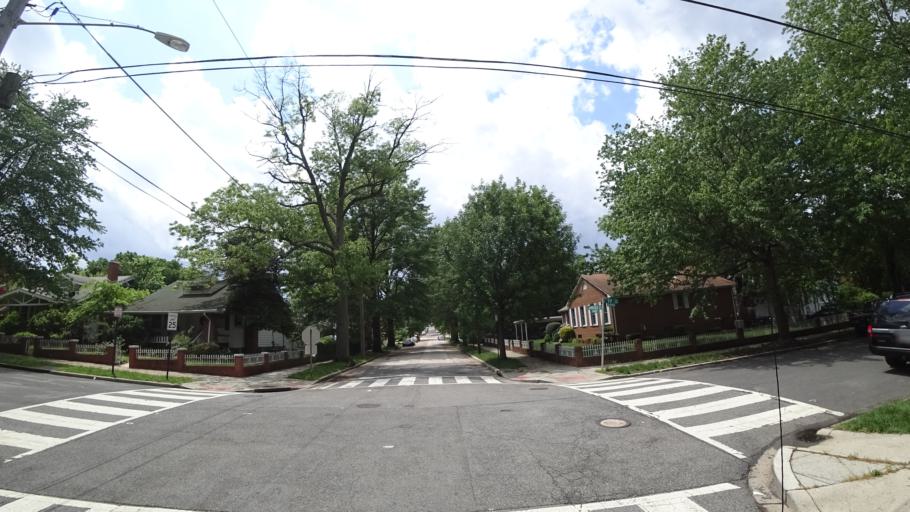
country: US
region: Maryland
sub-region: Prince George's County
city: Mount Rainier
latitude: 38.9321
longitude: -76.9810
